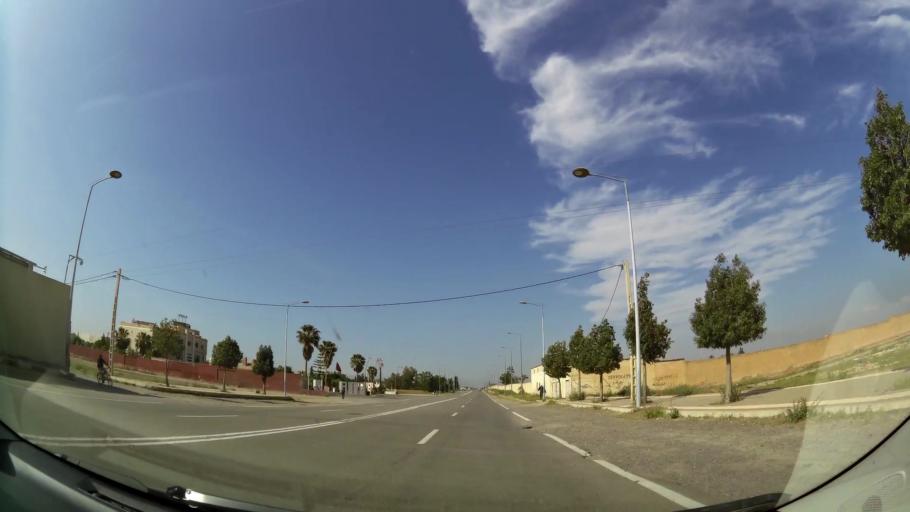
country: MA
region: Oriental
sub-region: Oujda-Angad
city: Oujda
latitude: 34.7196
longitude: -1.8814
